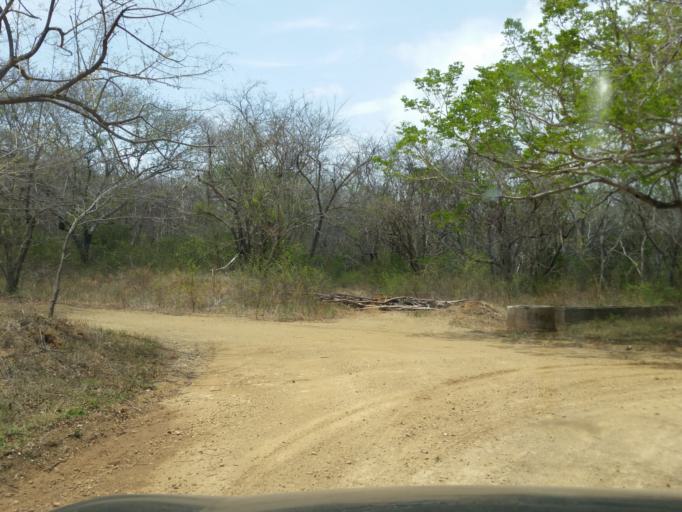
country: NI
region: Rivas
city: Tola
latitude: 11.4175
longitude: -86.0584
